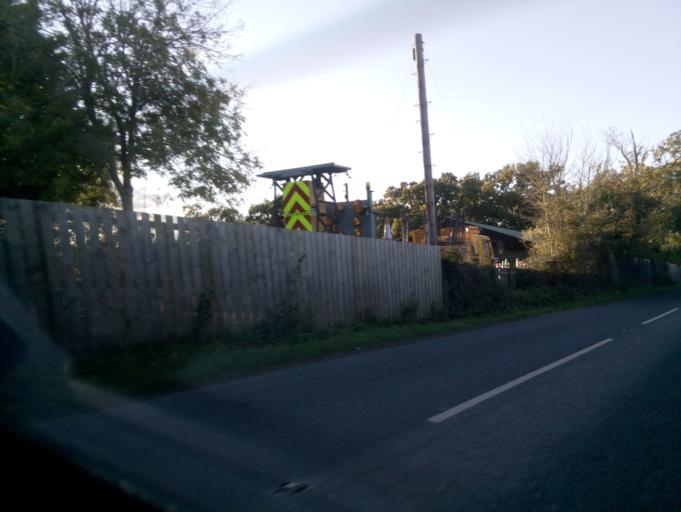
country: GB
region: England
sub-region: Worcestershire
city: Upton upon Severn
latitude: 52.0026
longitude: -2.2370
